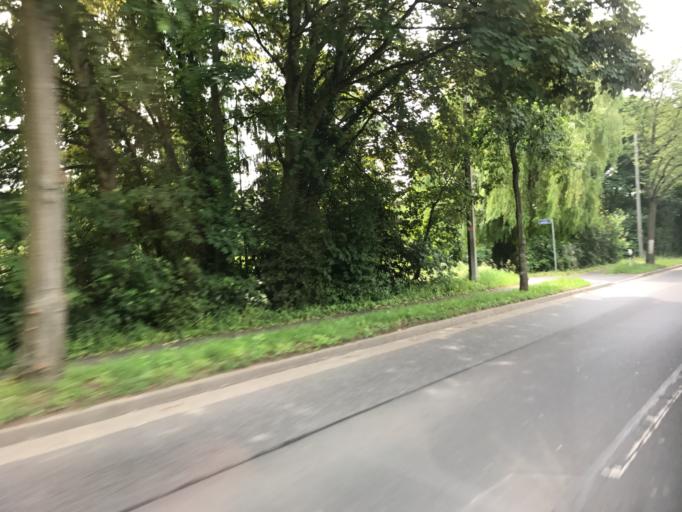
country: DE
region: Hesse
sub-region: Regierungsbezirk Darmstadt
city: Wiesbaden
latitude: 50.0553
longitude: 8.2086
